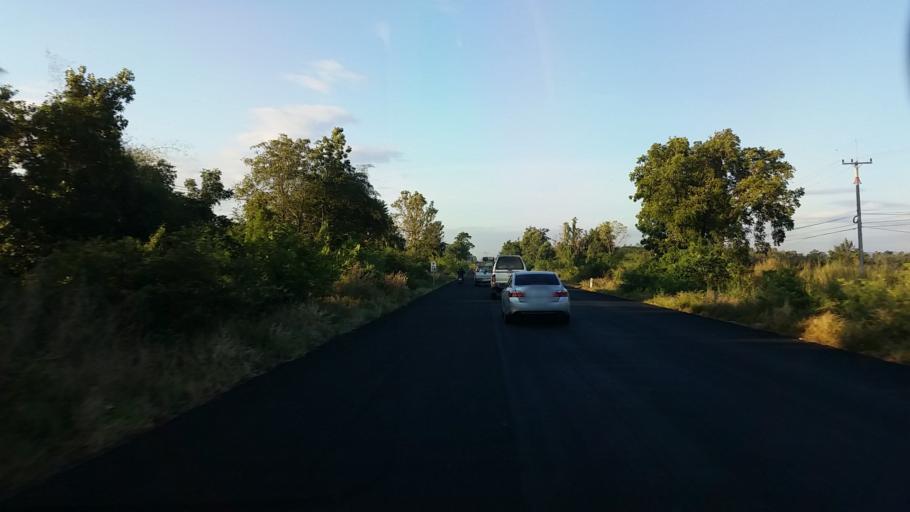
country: TH
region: Lop Buri
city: Chai Badan
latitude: 15.2347
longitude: 101.1593
